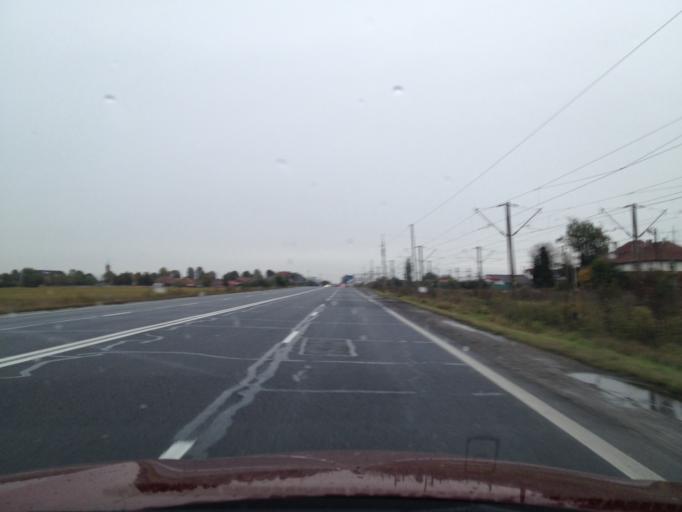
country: RO
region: Brasov
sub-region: Comuna Harman
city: Harman
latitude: 45.6976
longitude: 25.6851
